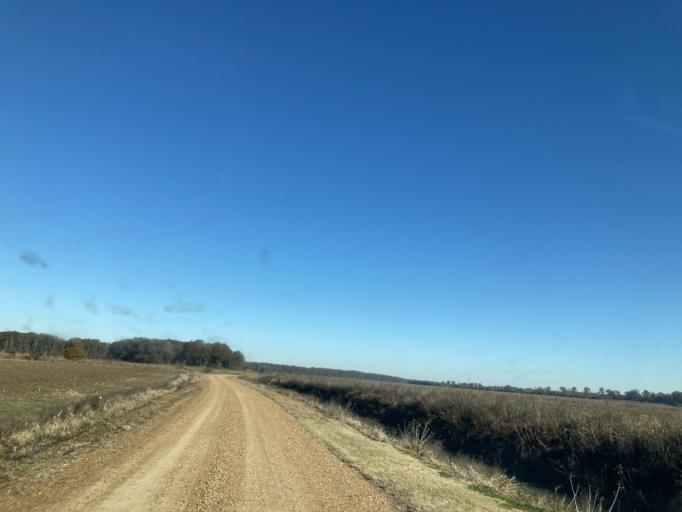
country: US
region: Mississippi
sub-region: Sharkey County
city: Rolling Fork
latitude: 32.8996
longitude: -90.6642
